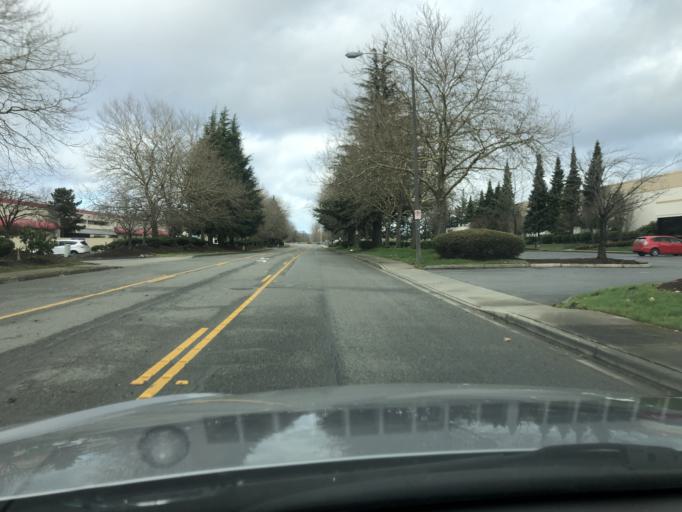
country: US
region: Washington
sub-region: King County
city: Kent
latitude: 47.4208
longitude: -122.2439
